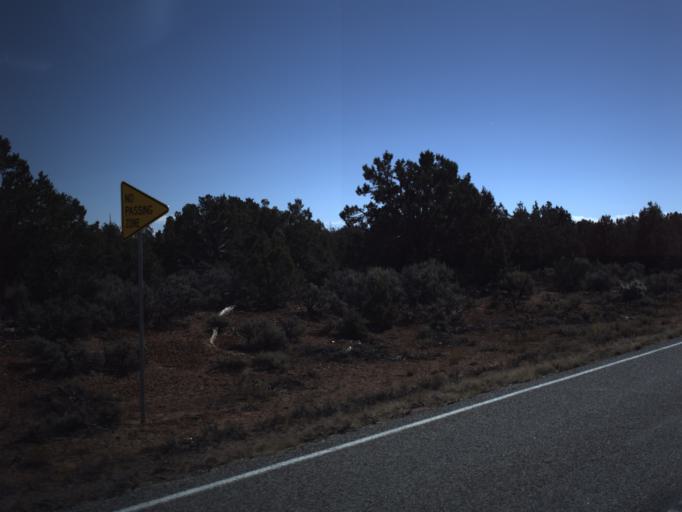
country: US
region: Utah
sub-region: San Juan County
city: Blanding
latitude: 37.3374
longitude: -109.9142
